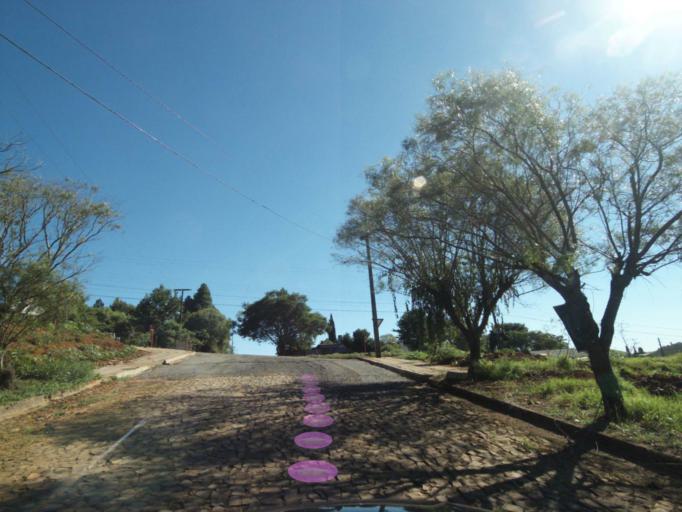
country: BR
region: Parana
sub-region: Coronel Vivida
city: Coronel Vivida
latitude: -26.1437
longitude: -52.3790
